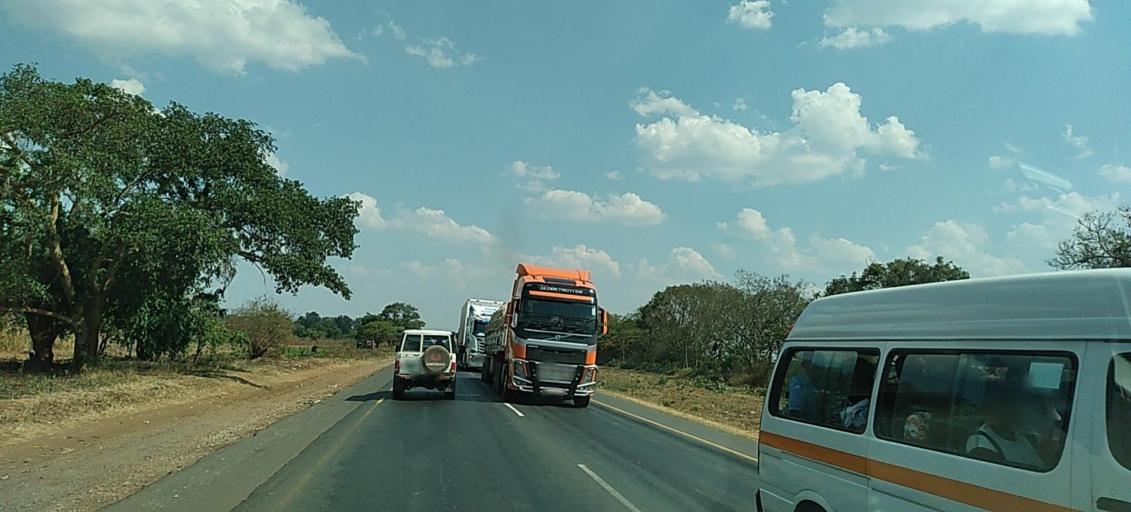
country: ZM
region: Central
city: Chibombo
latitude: -14.8820
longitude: 28.0618
